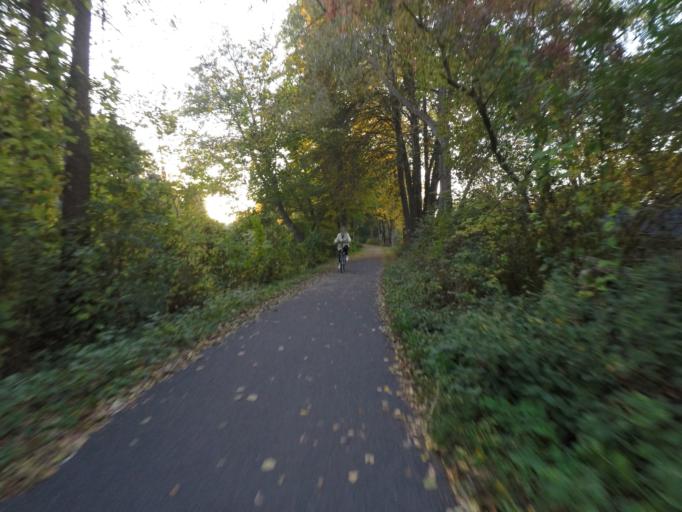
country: DE
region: Brandenburg
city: Melchow
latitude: 52.8457
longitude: 13.7058
